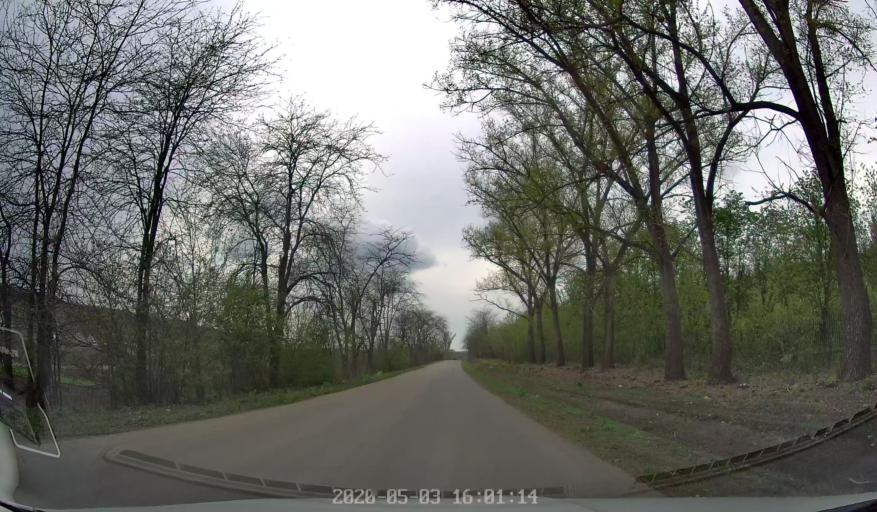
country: MD
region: Stinga Nistrului
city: Bucovat
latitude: 47.1646
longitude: 28.4115
